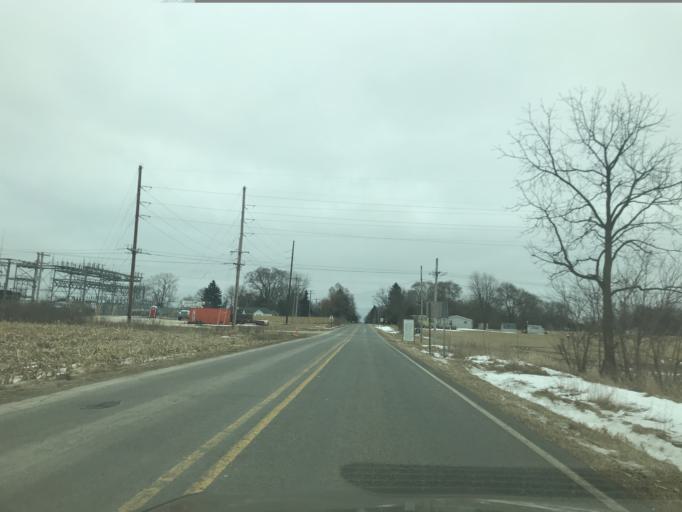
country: US
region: Michigan
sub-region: Jackson County
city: Brooklyn
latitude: 42.0734
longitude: -84.3367
